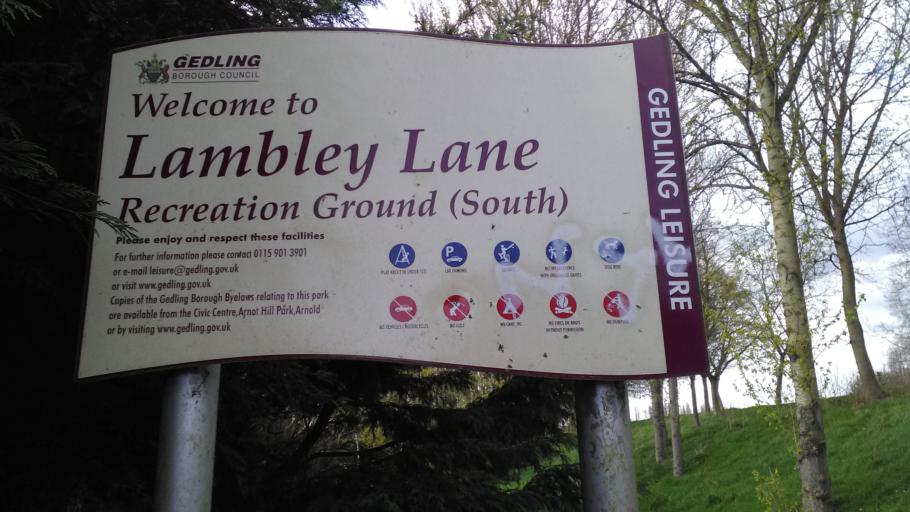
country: GB
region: England
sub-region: Nottinghamshire
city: Burton Joyce
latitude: 52.9811
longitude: -1.0830
